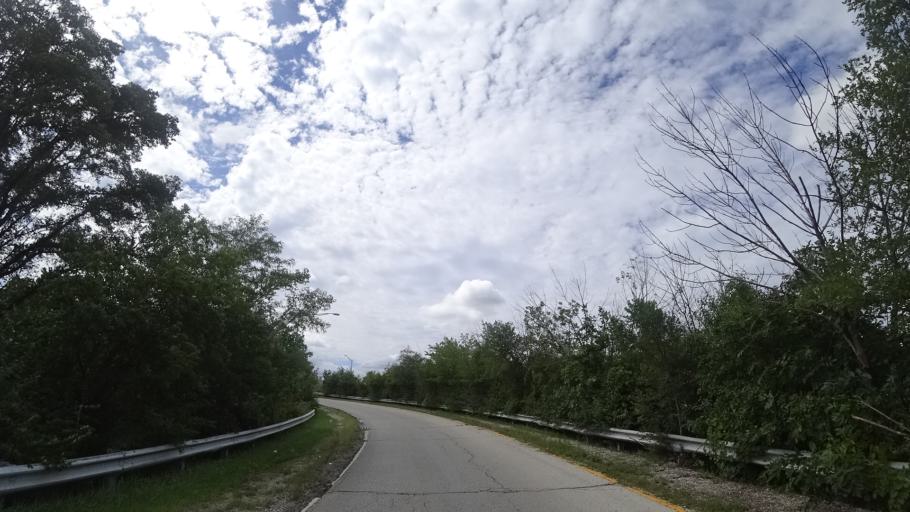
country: US
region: Illinois
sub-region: Cook County
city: Burbank
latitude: 41.7181
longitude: -87.7978
